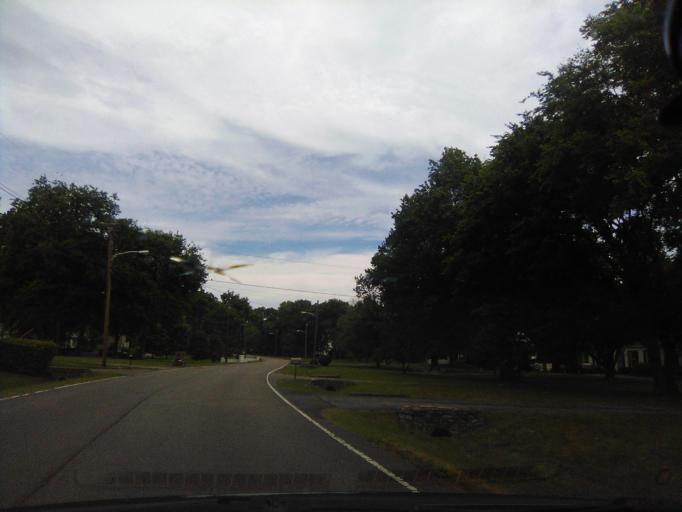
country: US
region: Tennessee
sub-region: Davidson County
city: Belle Meade
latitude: 36.0994
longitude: -86.8773
